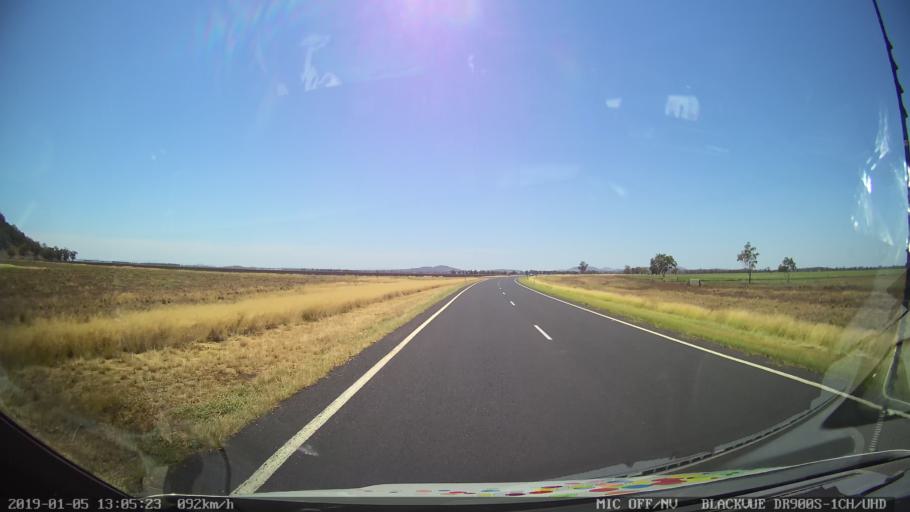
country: AU
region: New South Wales
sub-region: Gunnedah
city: Gunnedah
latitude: -31.0959
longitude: 149.8524
